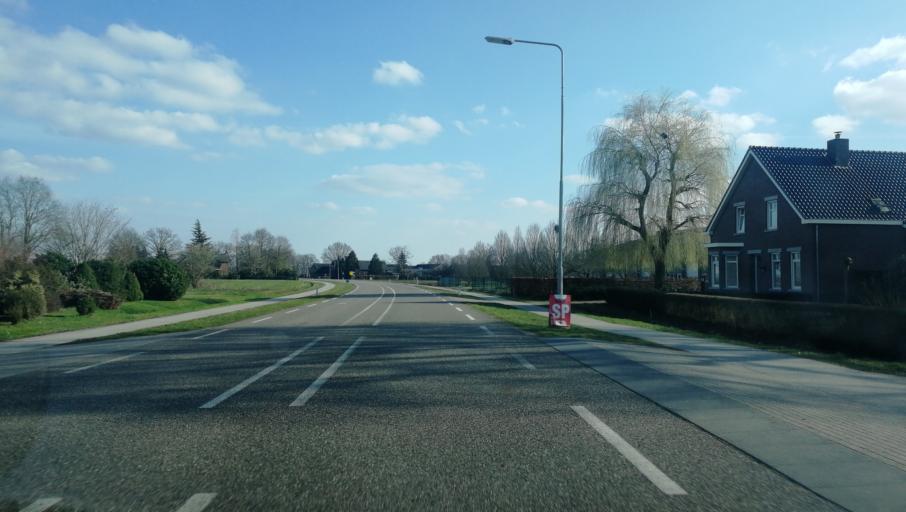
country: NL
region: Limburg
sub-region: Gemeente Peel en Maas
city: Maasbree
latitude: 51.4068
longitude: 6.0539
